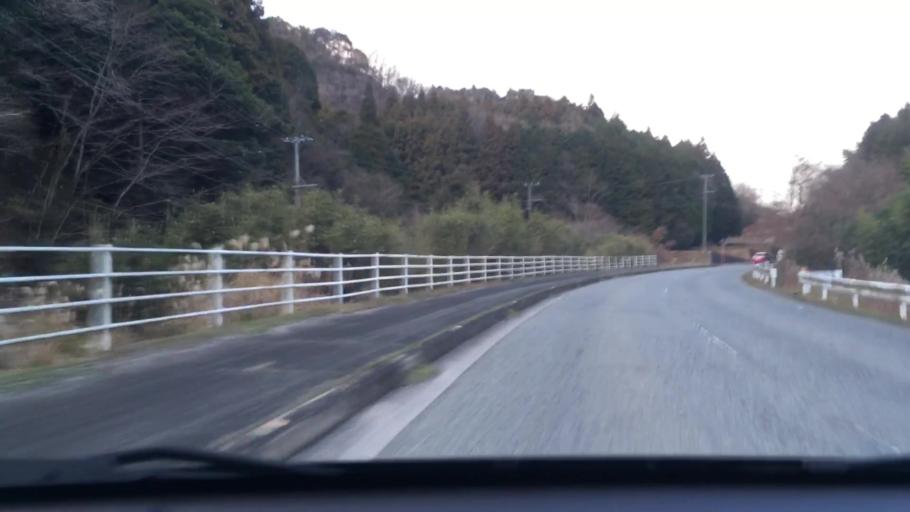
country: JP
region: Oita
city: Bungo-Takada-shi
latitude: 33.4731
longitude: 131.3842
